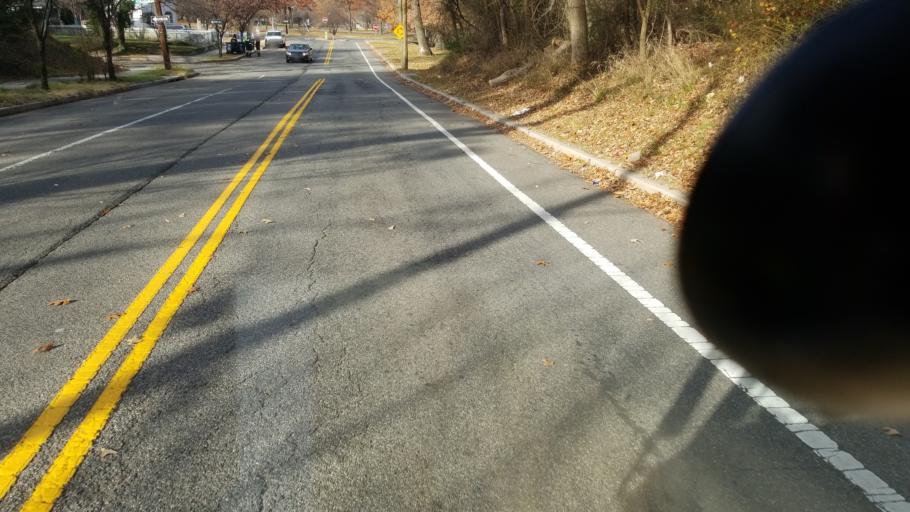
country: US
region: Maryland
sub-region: Prince George's County
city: Silver Hill
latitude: 38.8773
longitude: -76.9595
